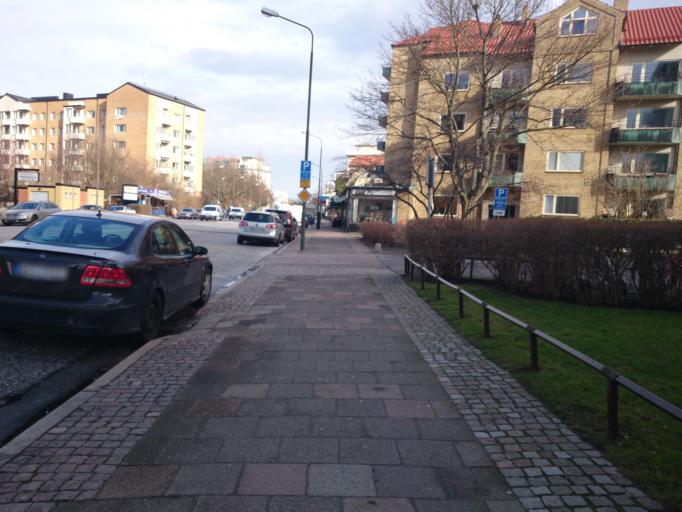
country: SE
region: Skane
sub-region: Malmo
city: Malmoe
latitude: 55.6011
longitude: 12.9769
